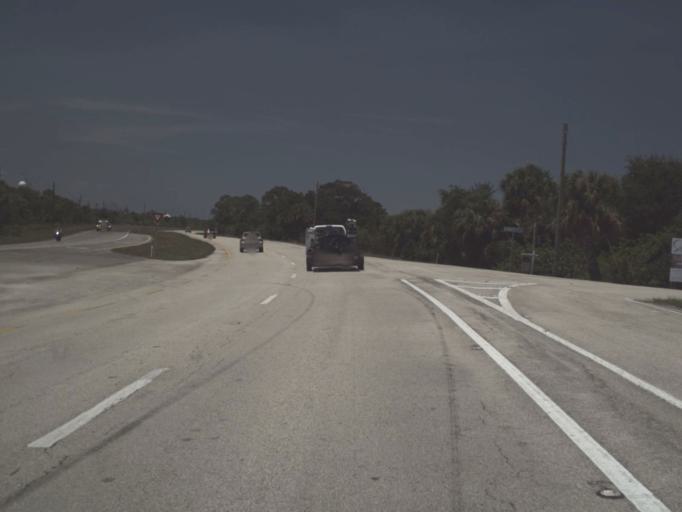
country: US
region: Florida
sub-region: Brevard County
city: Grant-Valkaria
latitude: 27.9694
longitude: -80.5449
